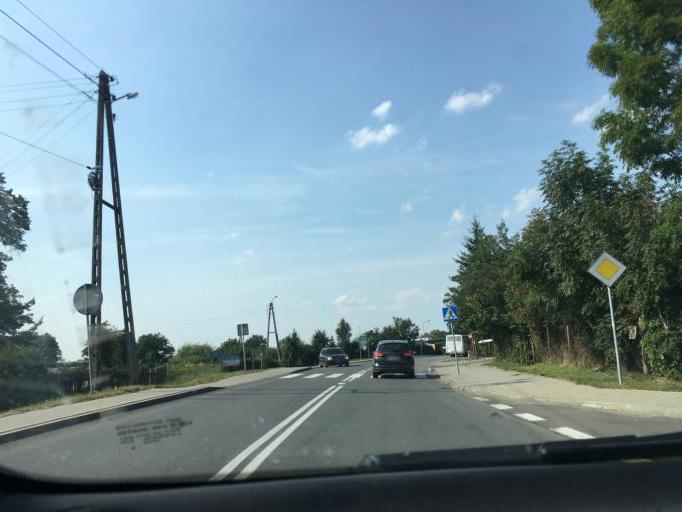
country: PL
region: Opole Voivodeship
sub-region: Powiat prudnicki
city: Prudnik
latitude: 50.3457
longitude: 17.5580
